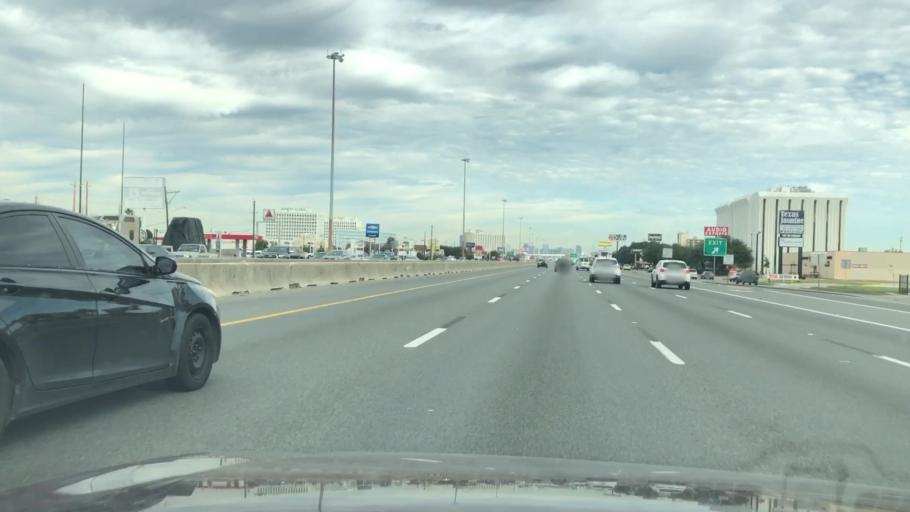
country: US
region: Texas
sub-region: Harris County
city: Bellaire
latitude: 29.7069
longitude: -95.5102
